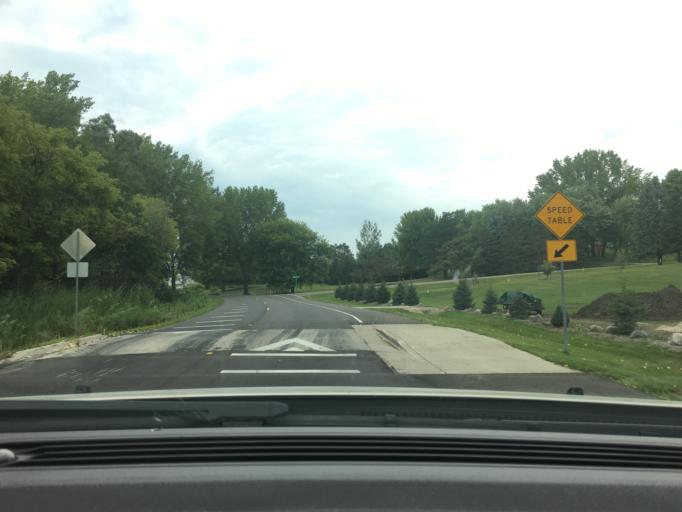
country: US
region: Minnesota
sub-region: Olmsted County
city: Rochester
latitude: 44.0834
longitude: -92.5190
